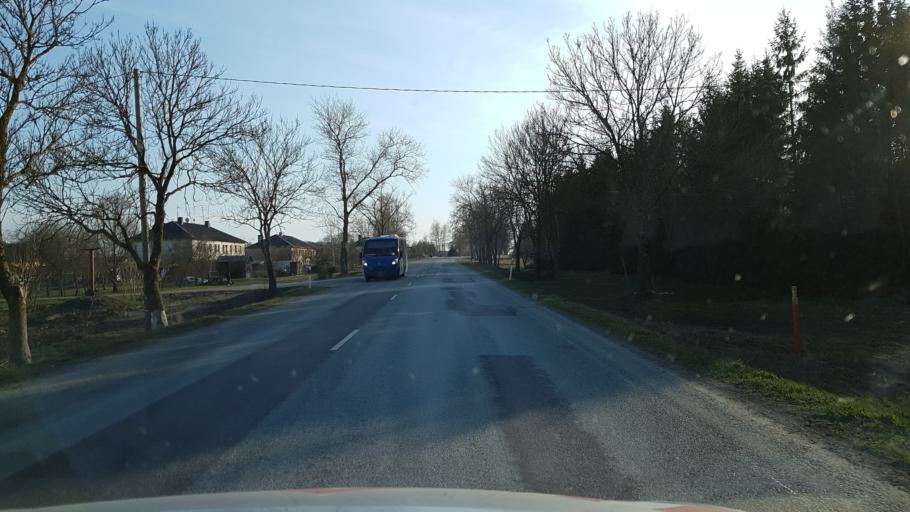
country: EE
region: Laeaene-Virumaa
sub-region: Rakvere linn
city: Rakvere
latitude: 59.3708
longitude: 26.3815
